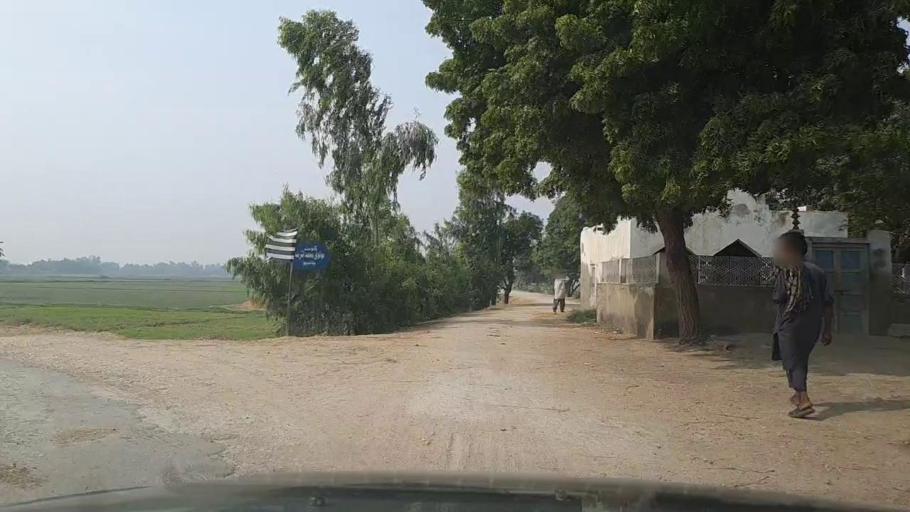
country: PK
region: Sindh
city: Mirpur Sakro
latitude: 24.5466
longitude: 67.8139
